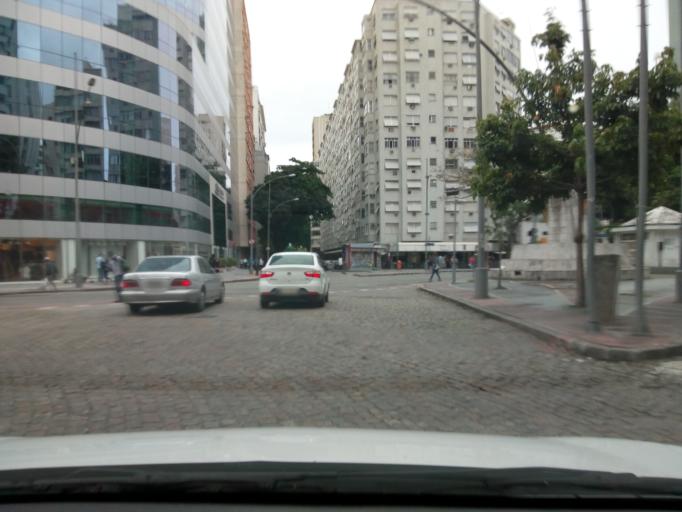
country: BR
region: Rio de Janeiro
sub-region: Rio De Janeiro
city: Rio de Janeiro
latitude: -22.9328
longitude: -43.1778
